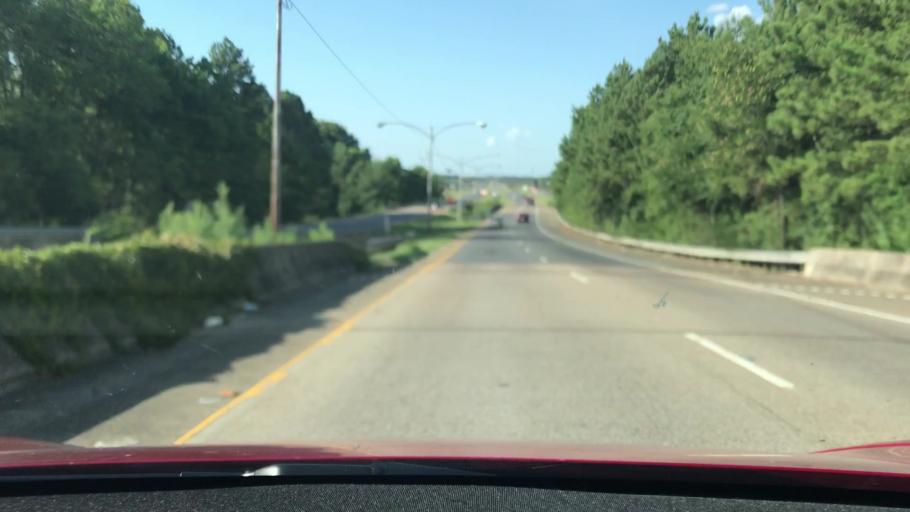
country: US
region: Louisiana
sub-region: Bossier Parish
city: Bossier City
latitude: 32.4315
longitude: -93.7842
